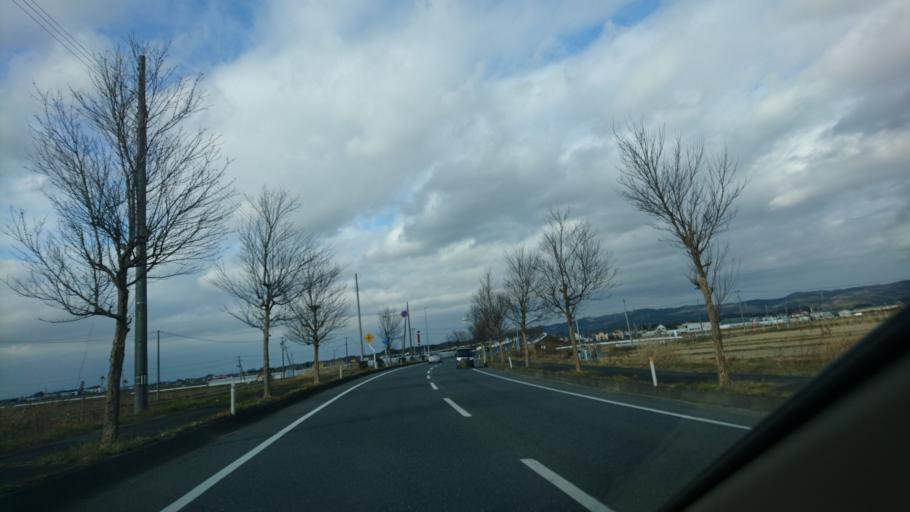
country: JP
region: Miyagi
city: Wakuya
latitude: 38.5423
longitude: 141.1087
